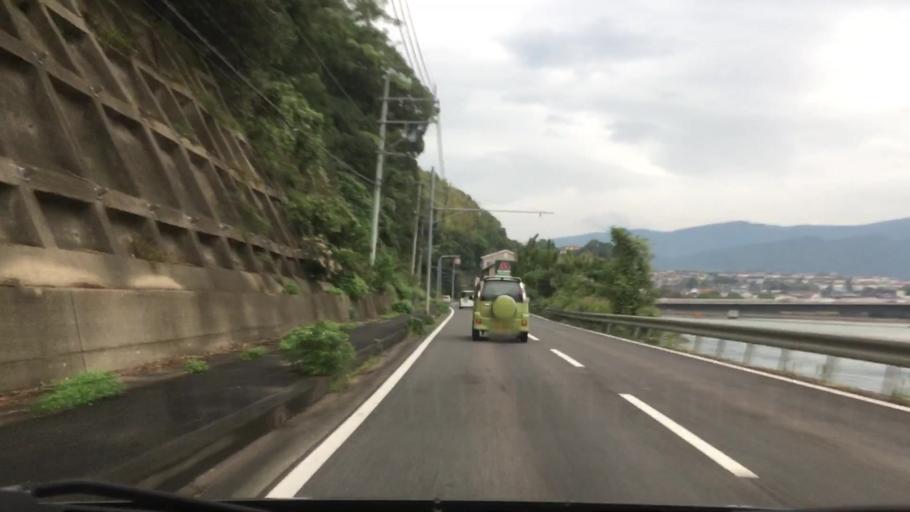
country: JP
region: Nagasaki
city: Sasebo
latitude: 33.1237
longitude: 129.7932
